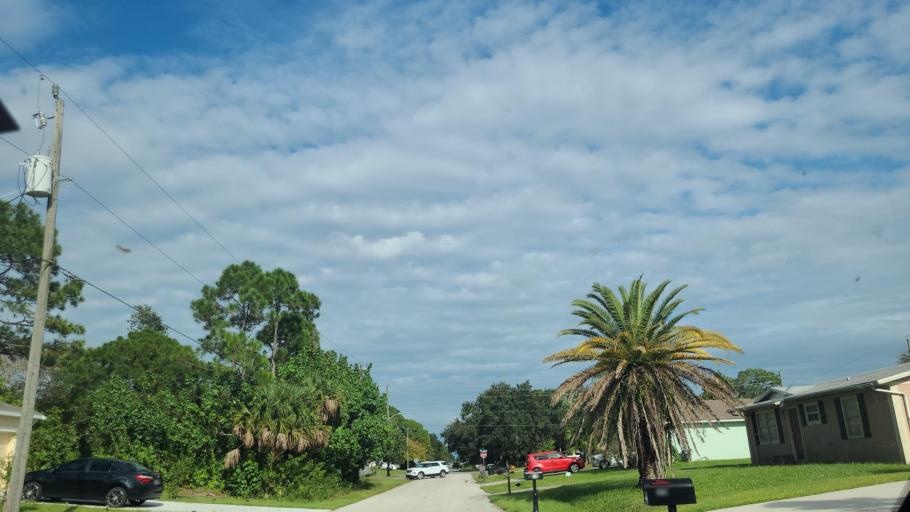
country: US
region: Florida
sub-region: Brevard County
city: West Melbourne
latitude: 27.9837
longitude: -80.6627
